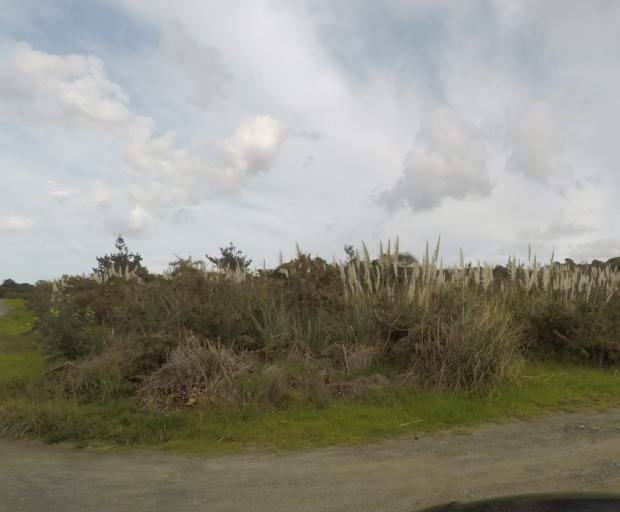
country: NZ
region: Northland
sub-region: Whangarei
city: Ruakaka
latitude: -35.9323
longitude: 174.4590
